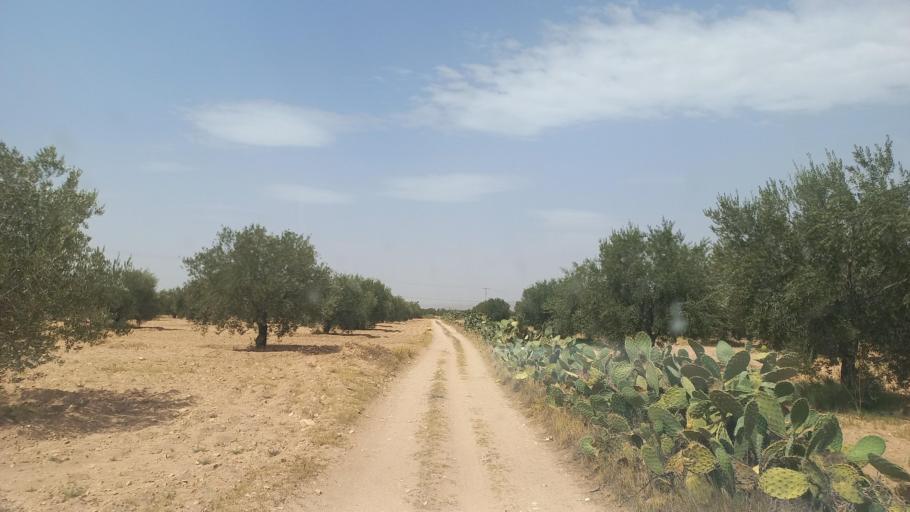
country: TN
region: Al Qasrayn
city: Kasserine
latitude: 35.2560
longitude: 9.0077
